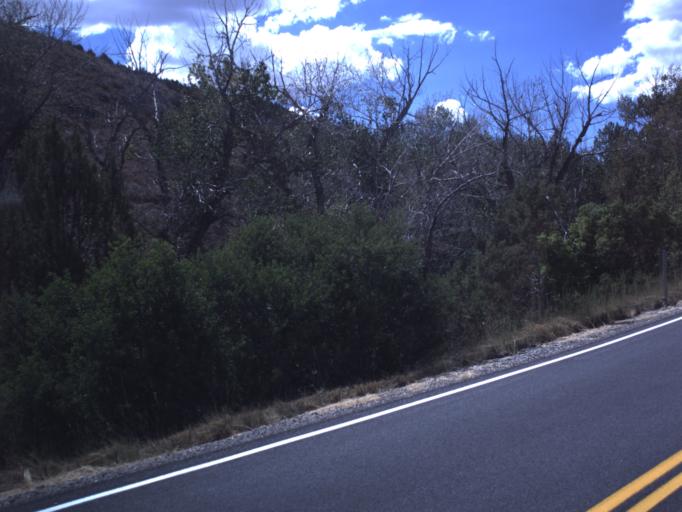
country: US
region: Utah
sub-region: Tooele County
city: Grantsville
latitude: 40.3432
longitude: -112.5437
